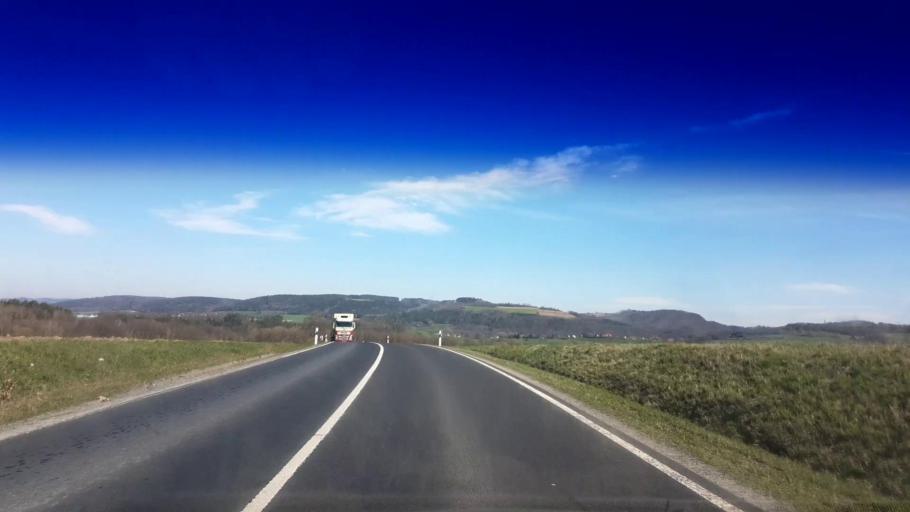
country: DE
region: Bavaria
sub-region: Upper Franconia
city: Gesees
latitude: 50.0174
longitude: 11.6354
